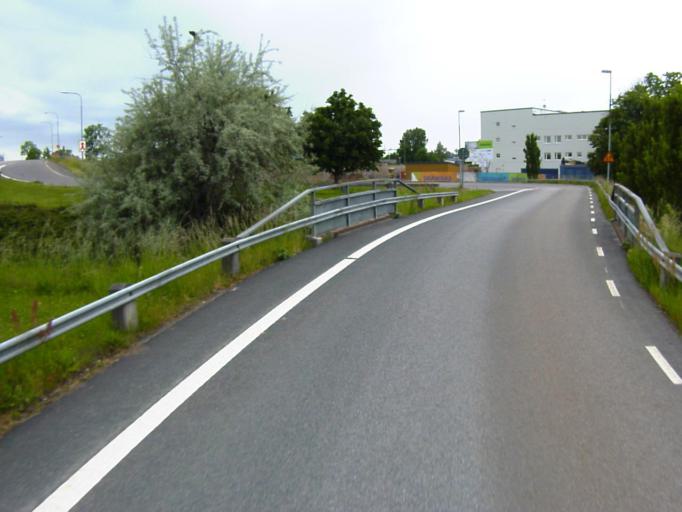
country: SE
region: Skane
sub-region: Kristianstads Kommun
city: Kristianstad
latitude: 56.0408
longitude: 14.1598
